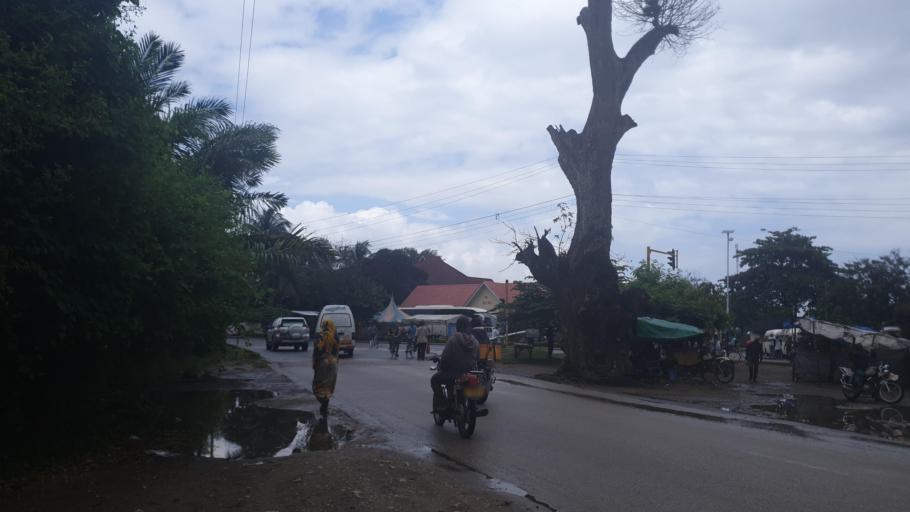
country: TZ
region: Tanga
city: Tanga
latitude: -5.0708
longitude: 39.0897
